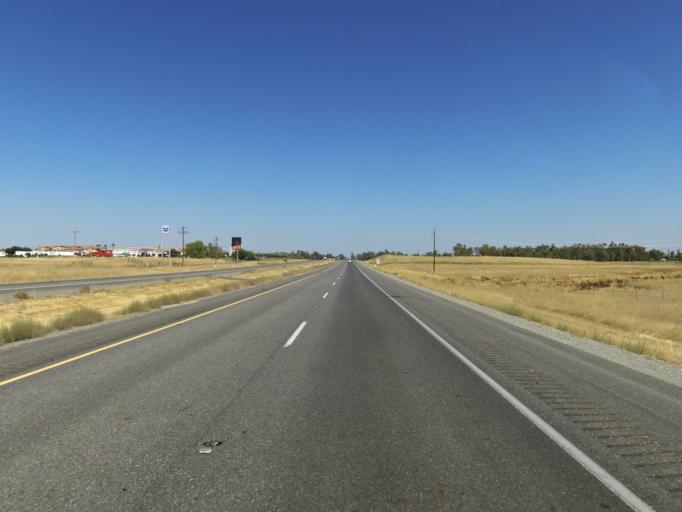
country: US
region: California
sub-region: Tehama County
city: Corning
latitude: 39.8693
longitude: -122.1999
